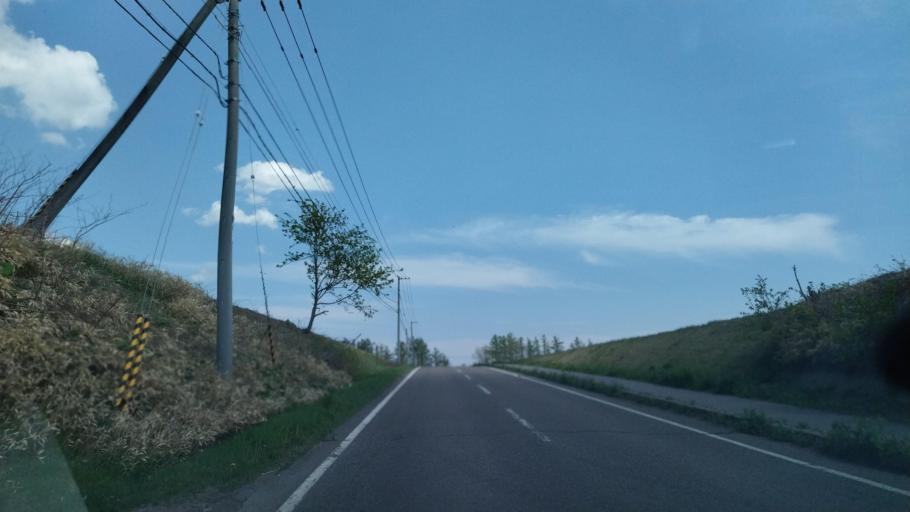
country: JP
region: Hokkaido
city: Otofuke
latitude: 43.1007
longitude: 143.2210
